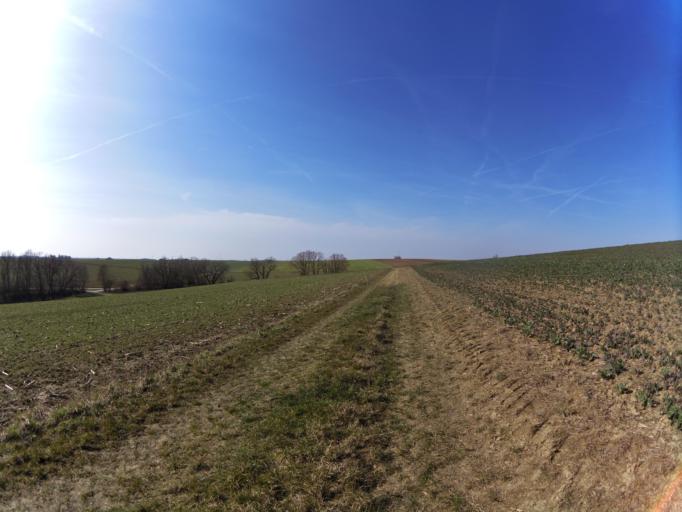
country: DE
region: Bavaria
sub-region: Regierungsbezirk Unterfranken
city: Dettelbach
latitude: 49.8267
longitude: 10.1416
